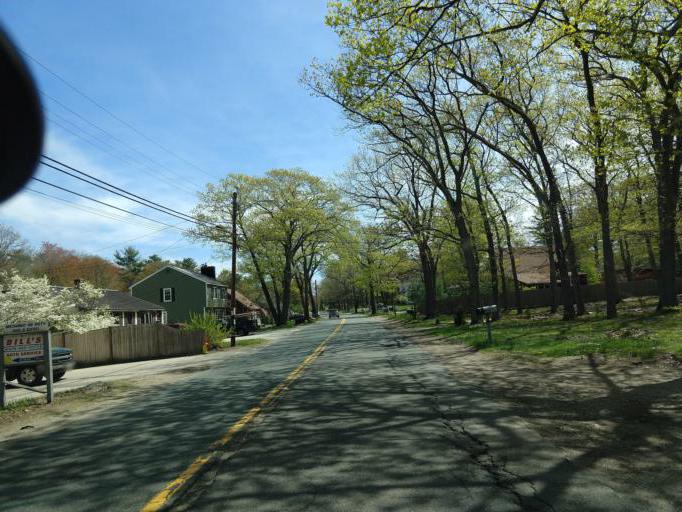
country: US
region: New Hampshire
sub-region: Rockingham County
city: Seabrook
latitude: 42.8685
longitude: -70.8746
